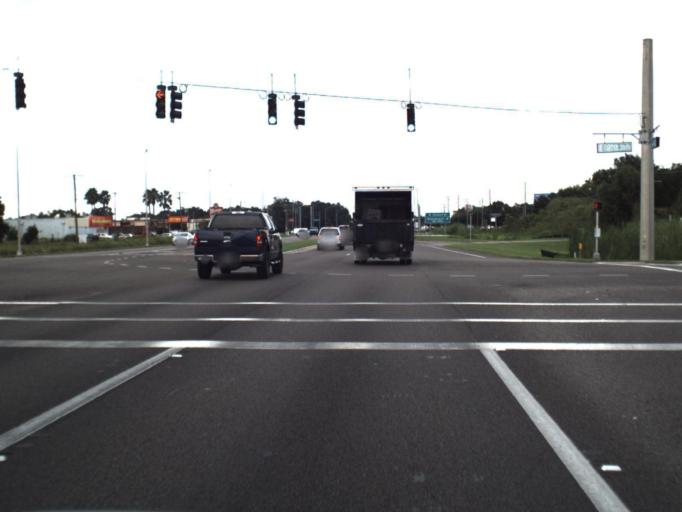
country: US
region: Florida
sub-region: Polk County
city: Medulla
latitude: 27.9345
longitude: -81.9740
